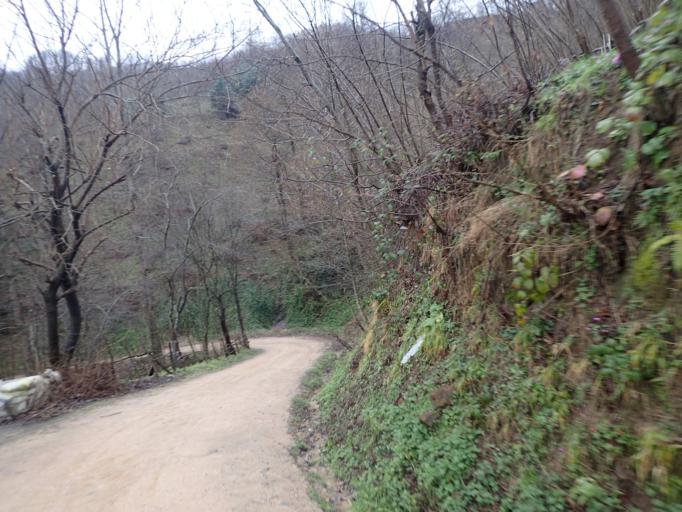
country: TR
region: Ordu
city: Camas
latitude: 40.9088
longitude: 37.5690
